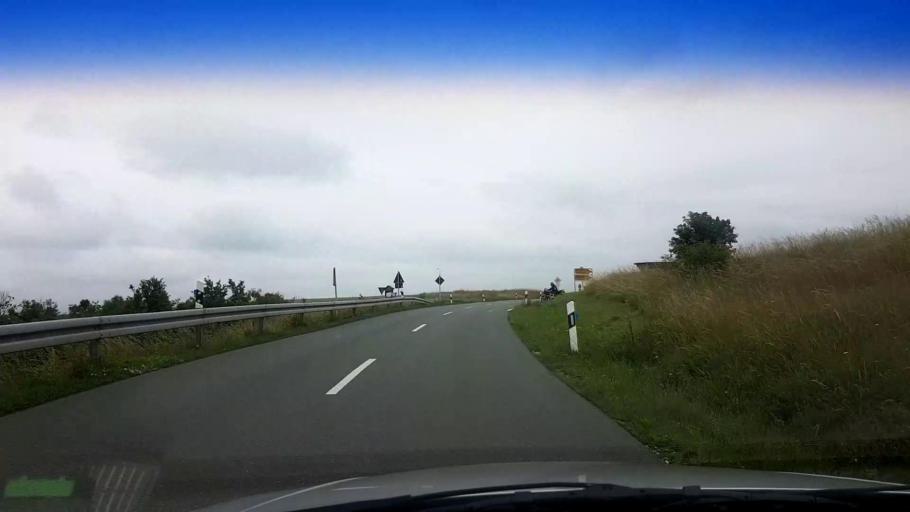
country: DE
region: Bavaria
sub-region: Upper Franconia
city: Mainleus
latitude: 50.0904
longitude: 11.3493
